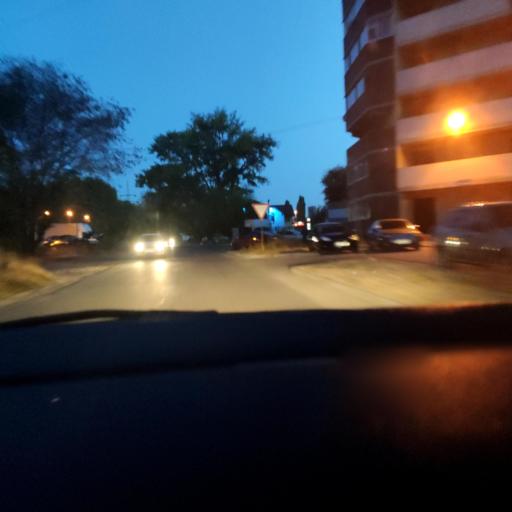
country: RU
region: Voronezj
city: Voronezh
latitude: 51.6712
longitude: 39.1653
